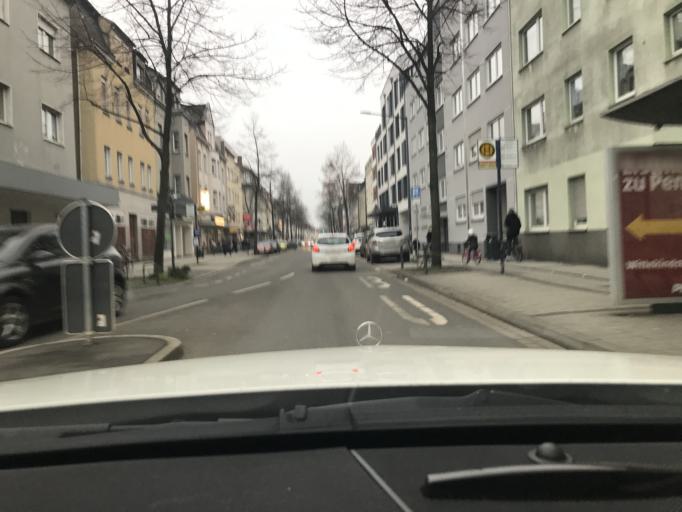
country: DE
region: North Rhine-Westphalia
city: Waltrop
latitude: 51.5979
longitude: 7.4382
